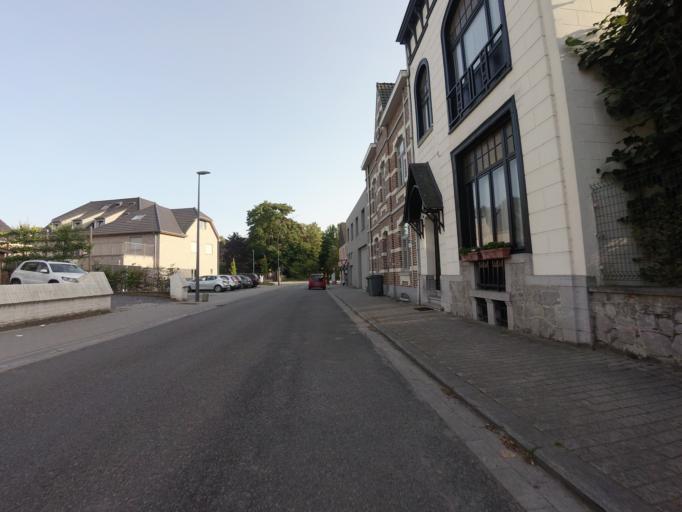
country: BE
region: Flanders
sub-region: Provincie Vlaams-Brabant
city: Kortenberg
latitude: 50.8896
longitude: 4.5464
